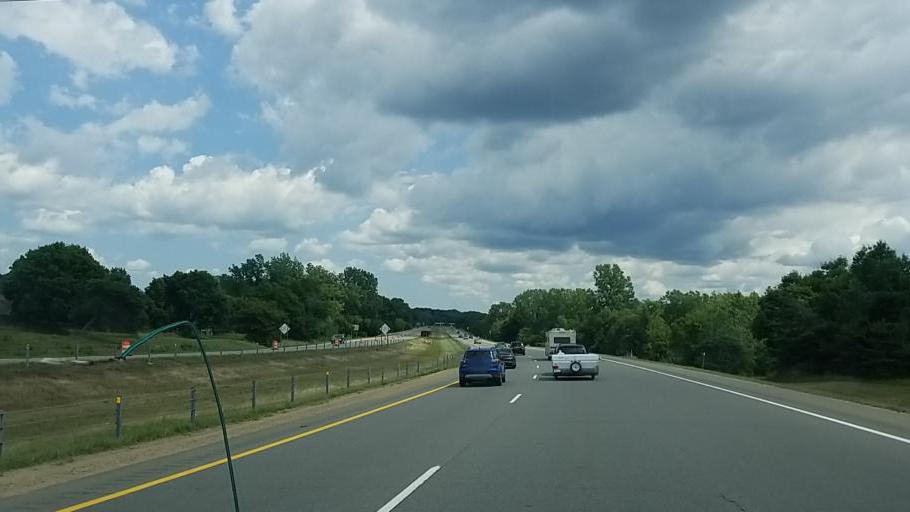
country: US
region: Michigan
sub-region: Kent County
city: Northview
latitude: 43.0175
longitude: -85.6327
